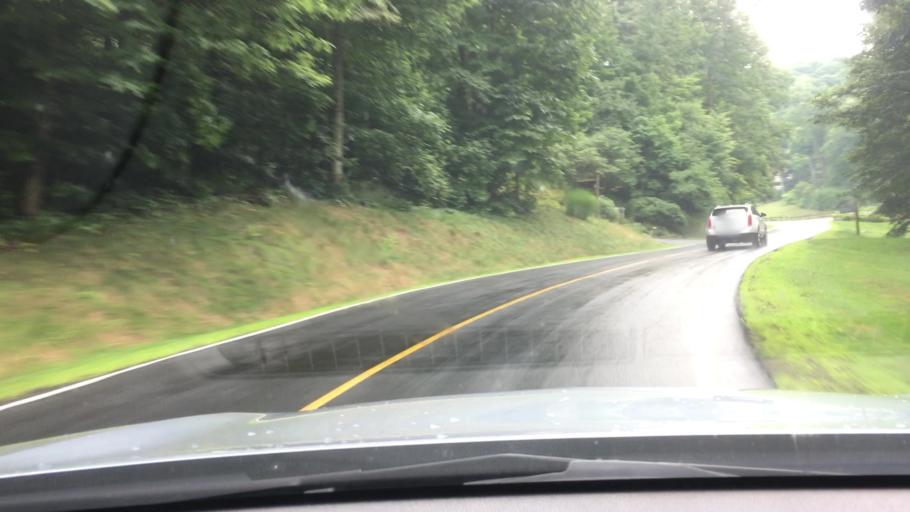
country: US
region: North Carolina
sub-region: Yancey County
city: Burnsville
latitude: 35.8800
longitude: -82.3479
